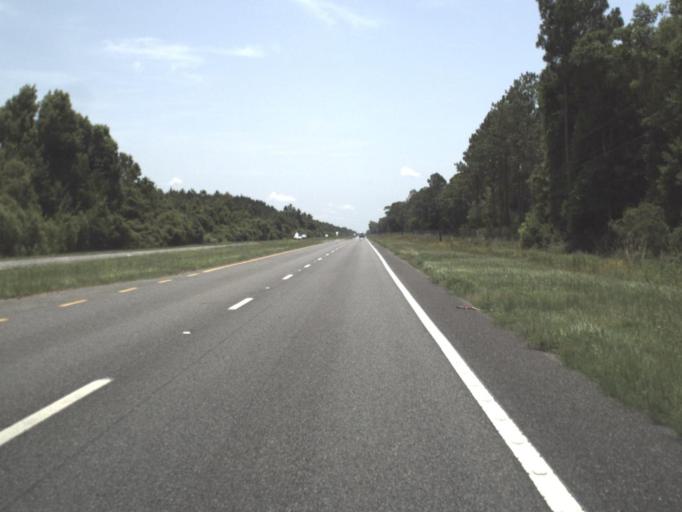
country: US
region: Florida
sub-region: Taylor County
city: Steinhatchee
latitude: 29.8671
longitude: -83.3952
